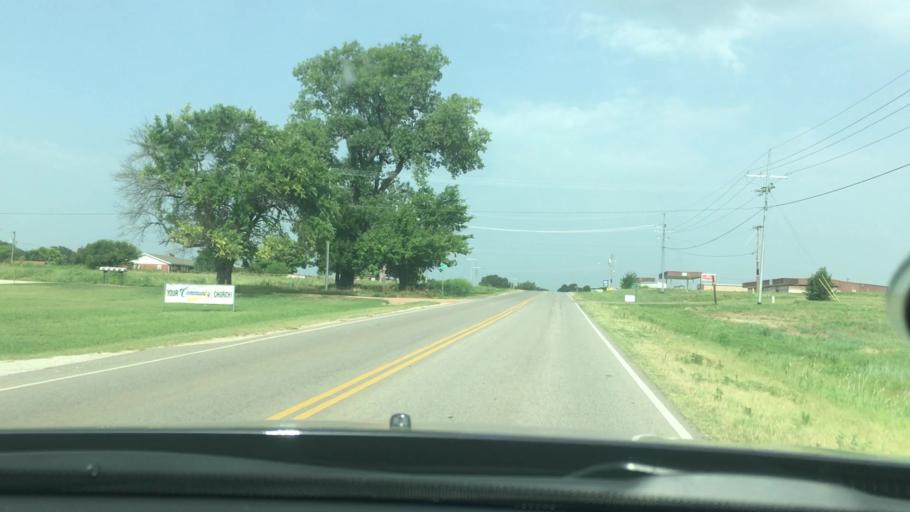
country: US
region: Oklahoma
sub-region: Pontotoc County
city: Ada
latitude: 34.7822
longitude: -96.7785
